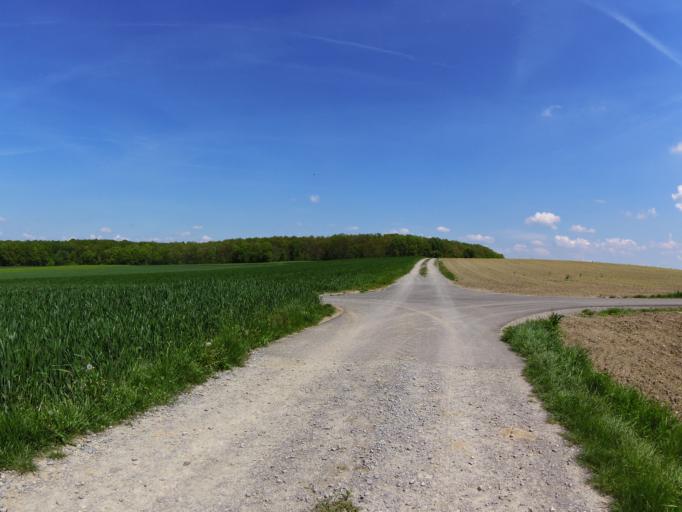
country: DE
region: Bavaria
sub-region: Regierungsbezirk Unterfranken
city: Theilheim
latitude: 49.7387
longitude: 10.0236
